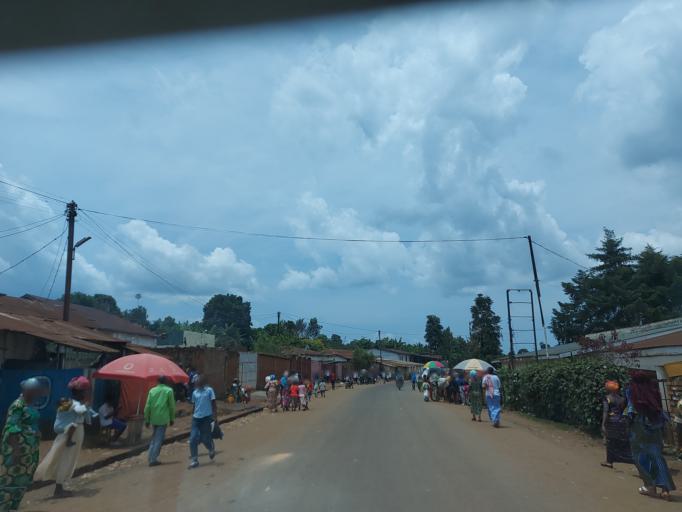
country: CD
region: South Kivu
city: Bukavu
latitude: -2.2951
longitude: 28.7995
